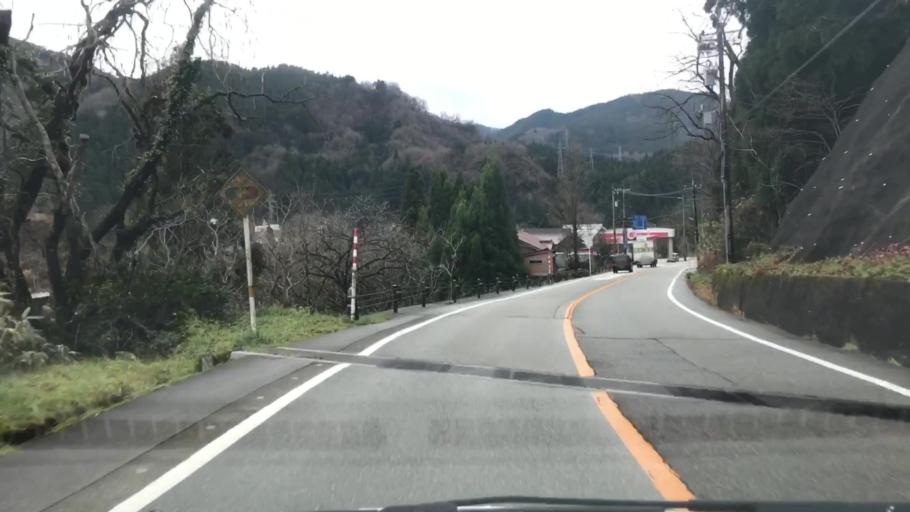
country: JP
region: Toyama
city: Kamiichi
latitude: 36.5758
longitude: 137.3795
